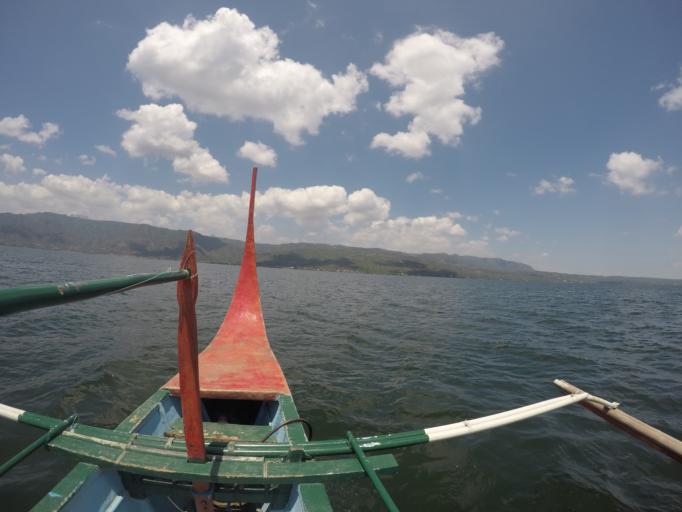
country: PH
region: Calabarzon
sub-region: Province of Batangas
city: Sampaloc
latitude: 14.0618
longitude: 120.9945
